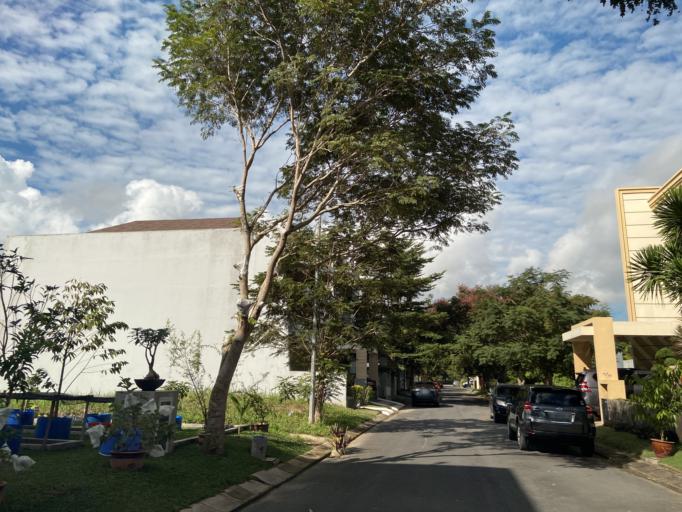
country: SG
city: Singapore
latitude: 1.0944
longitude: 104.0316
